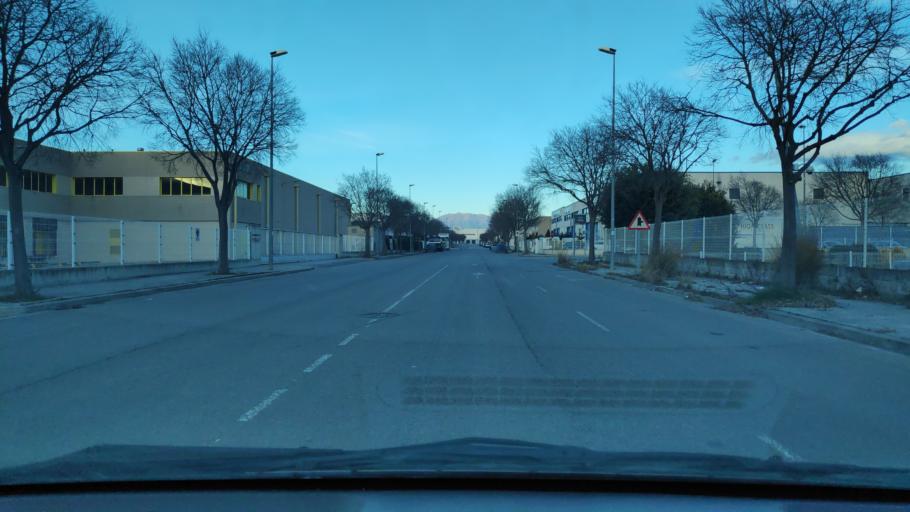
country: ES
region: Catalonia
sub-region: Provincia de Barcelona
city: Montmelo
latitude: 41.5681
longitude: 2.2653
